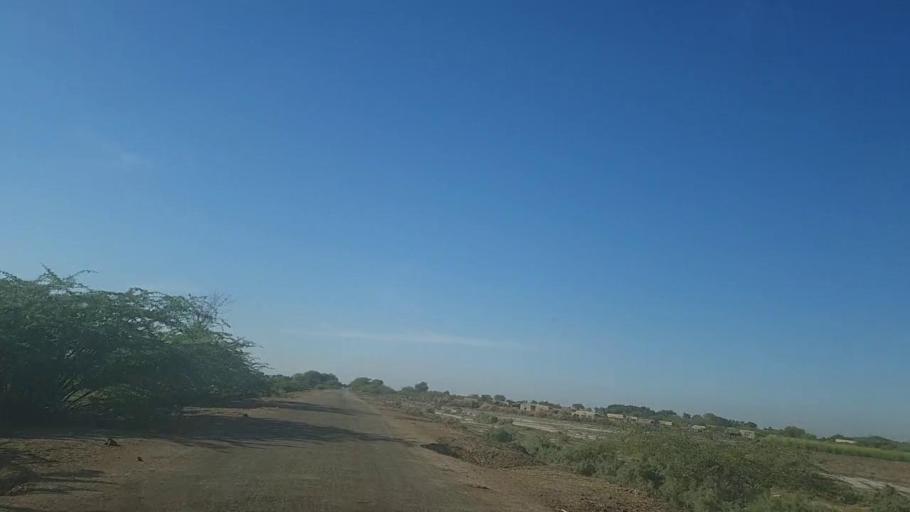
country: PK
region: Sindh
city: Pithoro
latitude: 25.5126
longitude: 69.3876
